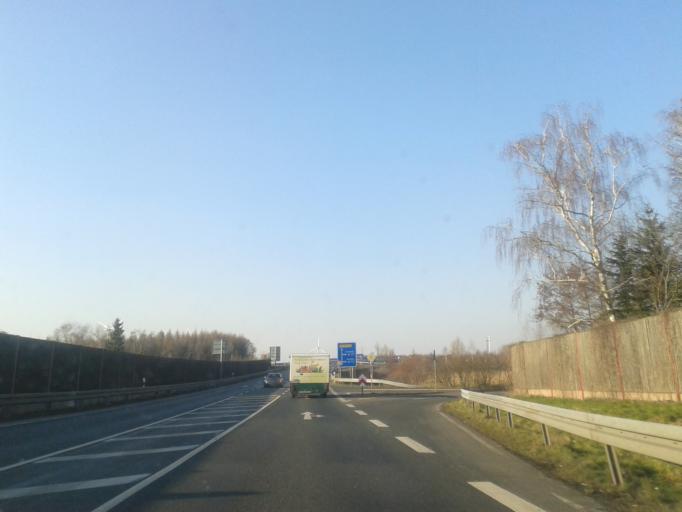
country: DE
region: Saxony
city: Nossen
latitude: 51.0326
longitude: 13.2941
